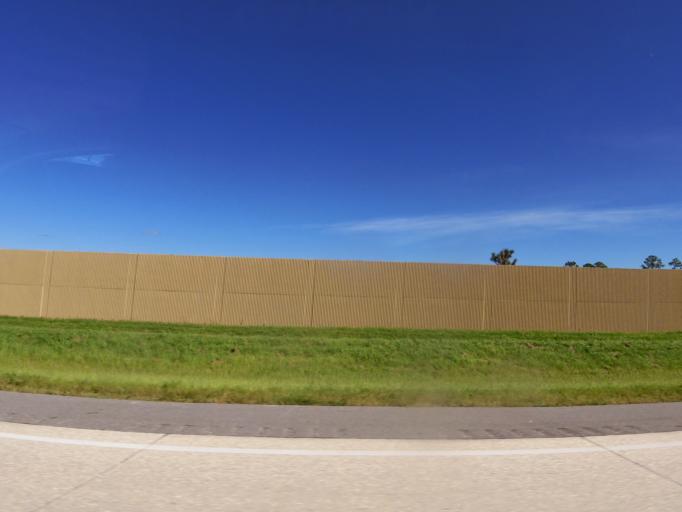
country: US
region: Florida
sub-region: Saint Johns County
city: Fruit Cove
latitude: 30.1250
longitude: -81.5114
